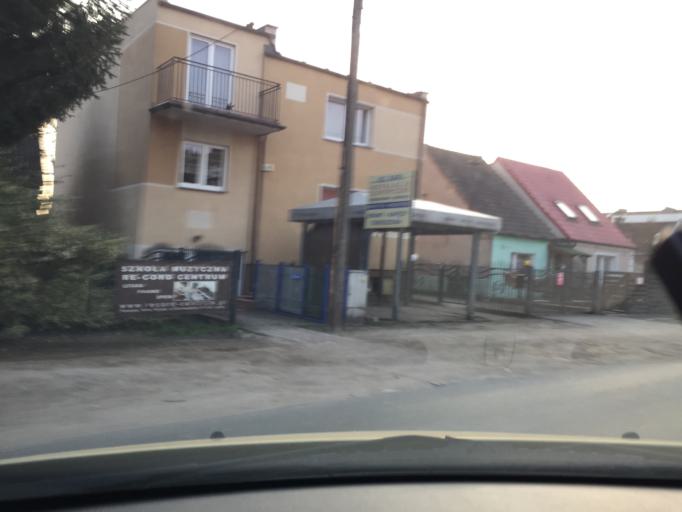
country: PL
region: Greater Poland Voivodeship
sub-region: Powiat poznanski
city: Plewiska
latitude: 52.3623
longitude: 16.8082
